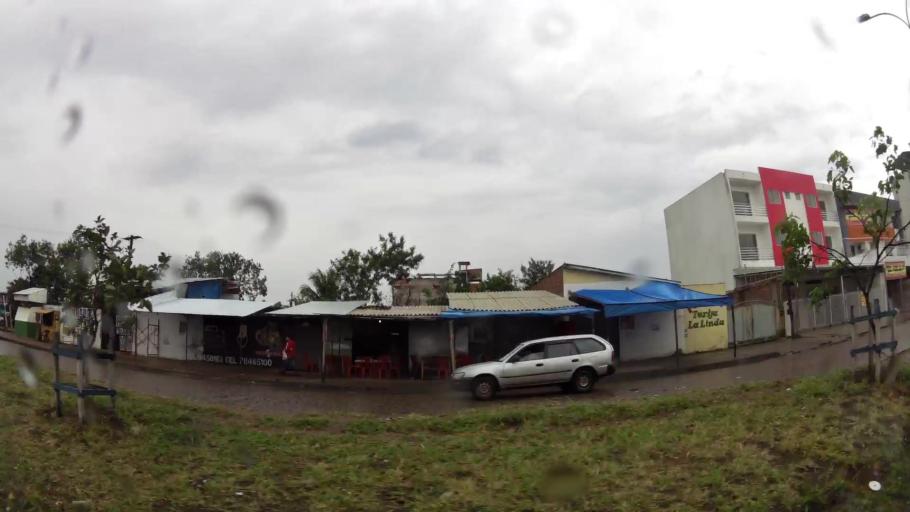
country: BO
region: Santa Cruz
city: Santa Cruz de la Sierra
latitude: -17.7932
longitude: -63.1626
